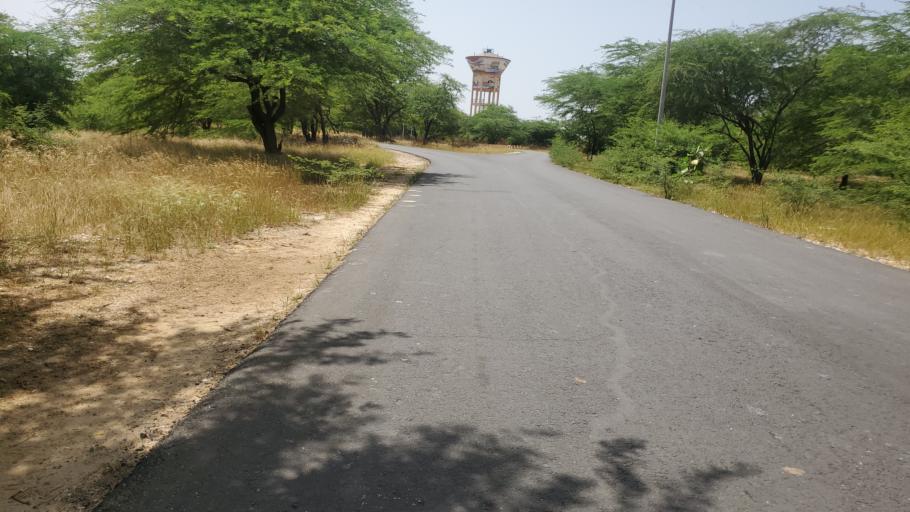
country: SN
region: Saint-Louis
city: Saint-Louis
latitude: 16.0593
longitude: -16.4256
